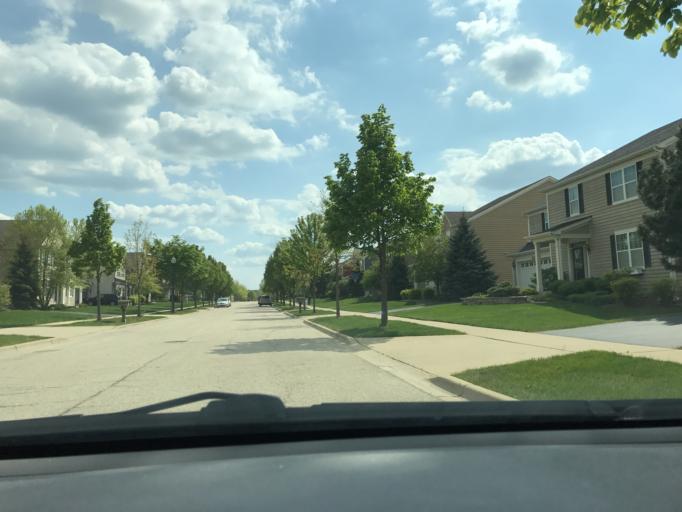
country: US
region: Illinois
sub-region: Kane County
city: Pingree Grove
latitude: 42.0364
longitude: -88.3595
